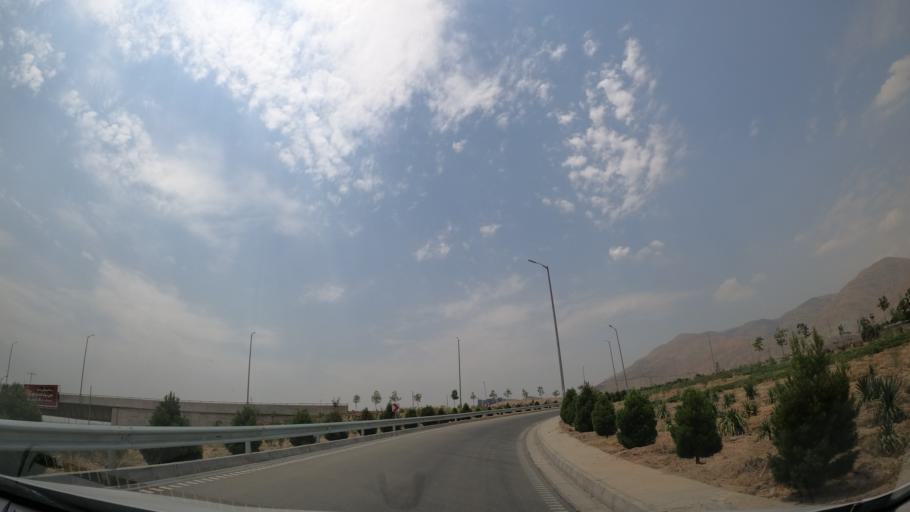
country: IR
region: Tehran
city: Shahr-e Qods
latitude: 35.7443
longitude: 51.1286
